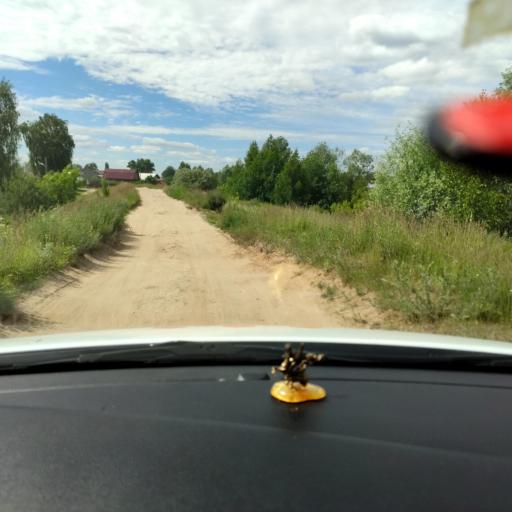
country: RU
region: Tatarstan
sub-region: Zelenodol'skiy Rayon
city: Vasil'yevo
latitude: 55.8366
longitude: 48.7194
